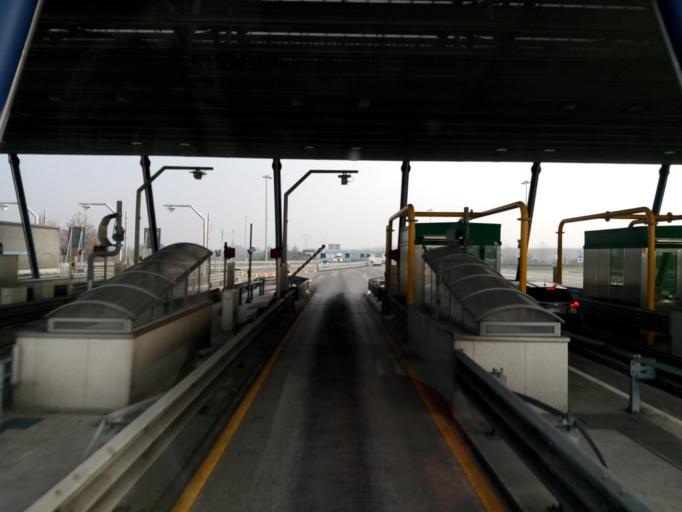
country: IT
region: Friuli Venezia Giulia
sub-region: Provincia di Pordenone
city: Cavolano-Schiavoi
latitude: 45.9212
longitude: 12.4787
